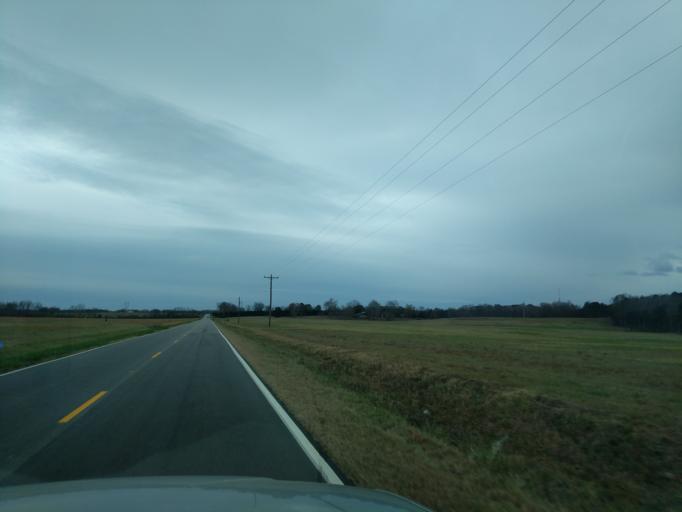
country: US
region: South Carolina
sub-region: Laurens County
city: Laurens
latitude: 34.3667
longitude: -81.9928
